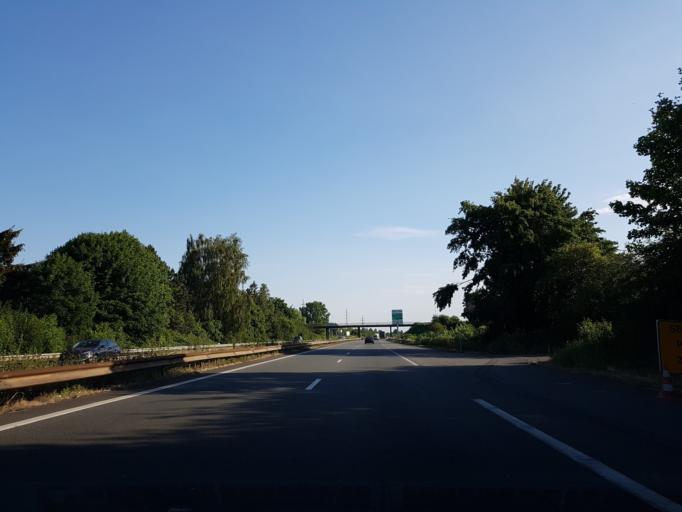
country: FR
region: Nord-Pas-de-Calais
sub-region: Departement du Nord
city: Lieu-Saint-Amand
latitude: 50.2659
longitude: 3.3318
